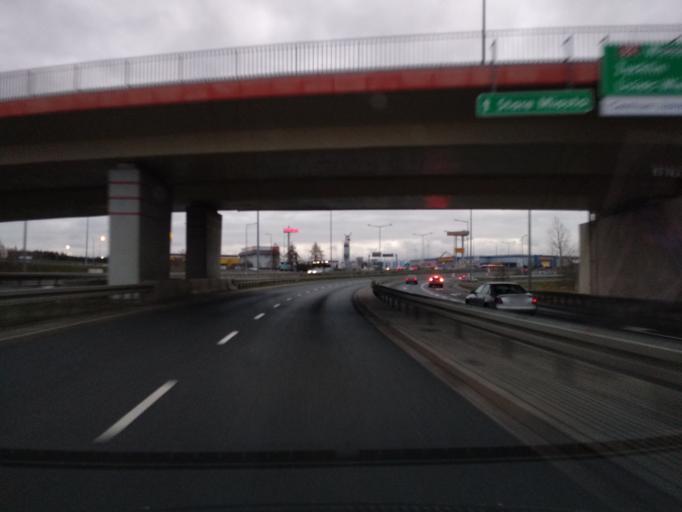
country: PL
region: Greater Poland Voivodeship
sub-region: Powiat koninski
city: Stare Miasto
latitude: 52.1883
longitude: 18.2281
